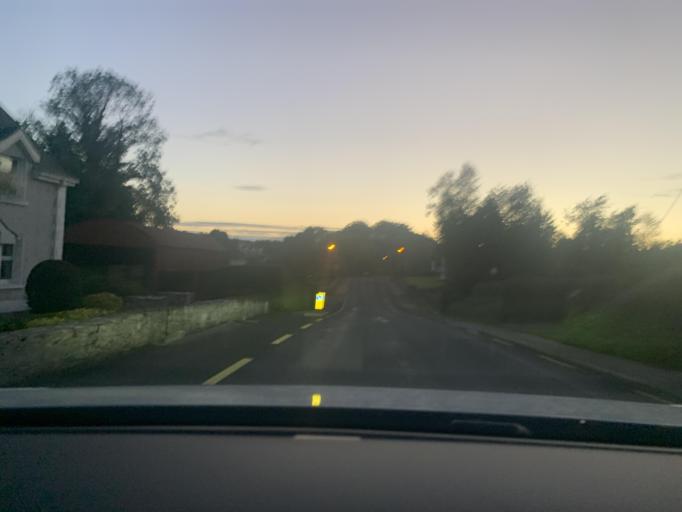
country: IE
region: Connaught
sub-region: Sligo
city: Sligo
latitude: 54.2836
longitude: -8.3956
